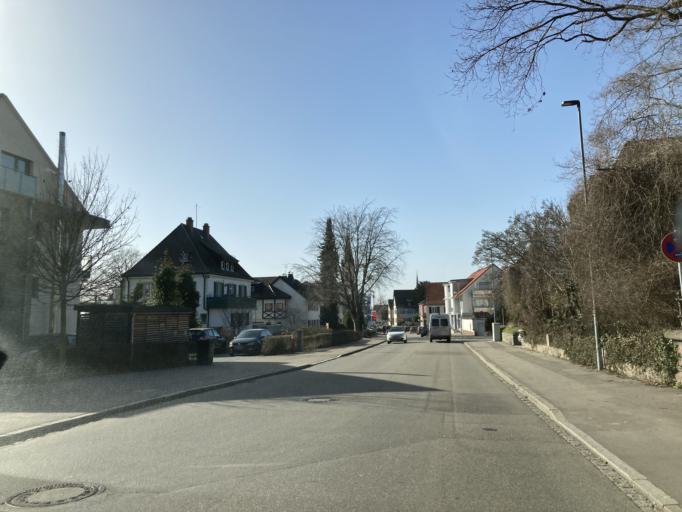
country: DE
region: Baden-Wuerttemberg
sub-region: Freiburg Region
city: Mullheim
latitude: 47.8085
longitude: 7.6346
